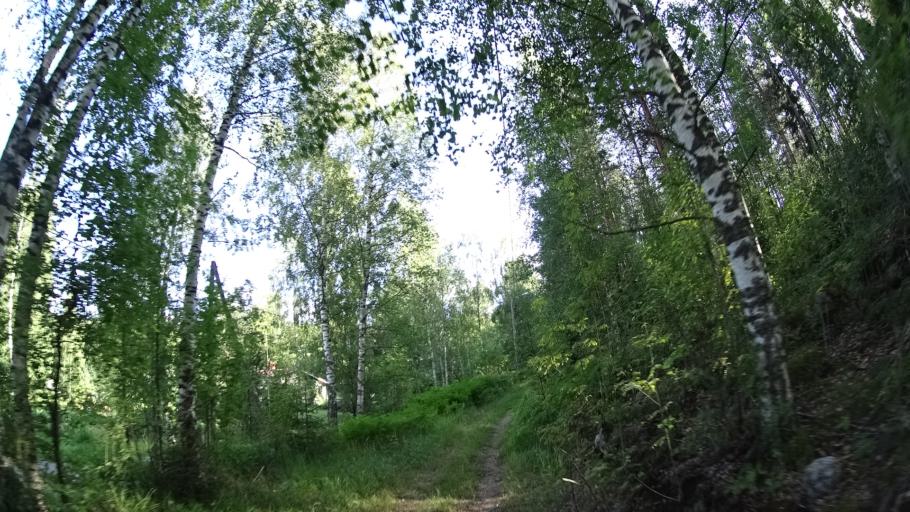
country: FI
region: Uusimaa
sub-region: Helsinki
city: Vihti
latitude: 60.3766
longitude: 24.3837
